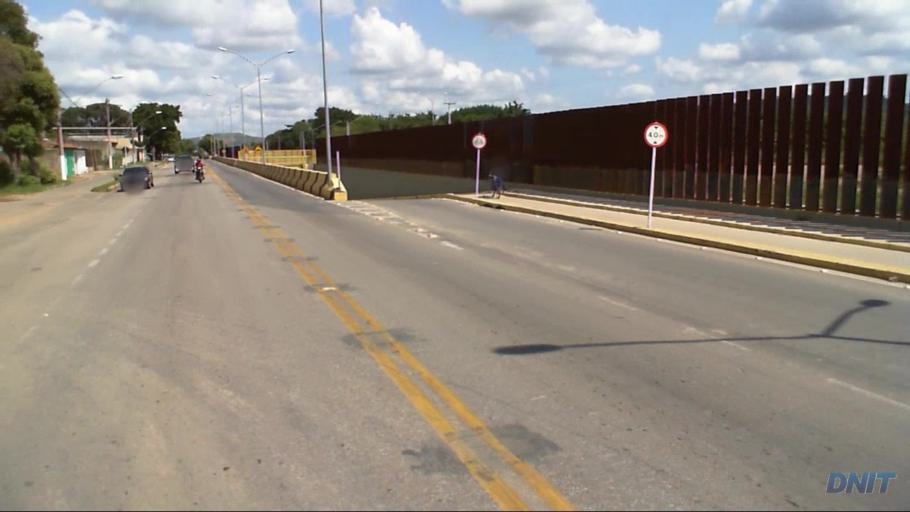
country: BR
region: Minas Gerais
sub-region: Governador Valadares
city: Governador Valadares
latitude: -18.9033
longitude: -41.9881
